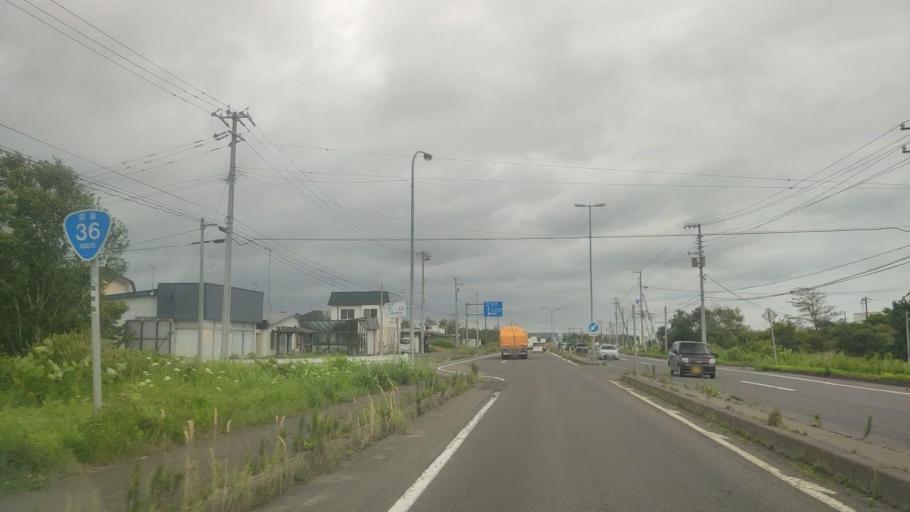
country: JP
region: Hokkaido
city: Shiraoi
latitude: 42.5279
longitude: 141.3207
